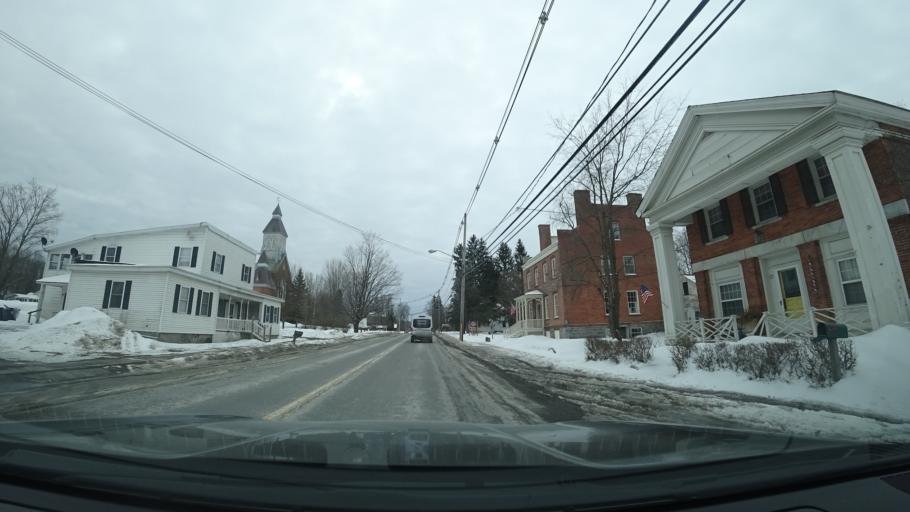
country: US
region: New York
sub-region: Washington County
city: Fort Edward
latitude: 43.2357
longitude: -73.4908
